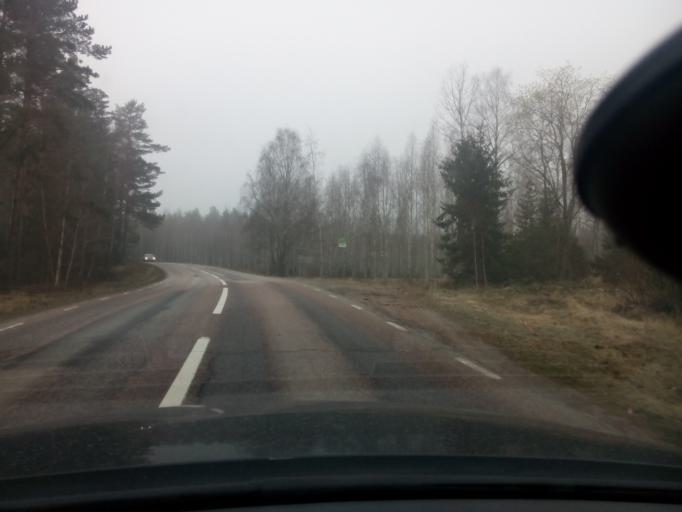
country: SE
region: Soedermanland
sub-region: Nykopings Kommun
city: Nykoping
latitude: 58.8793
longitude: 17.0882
